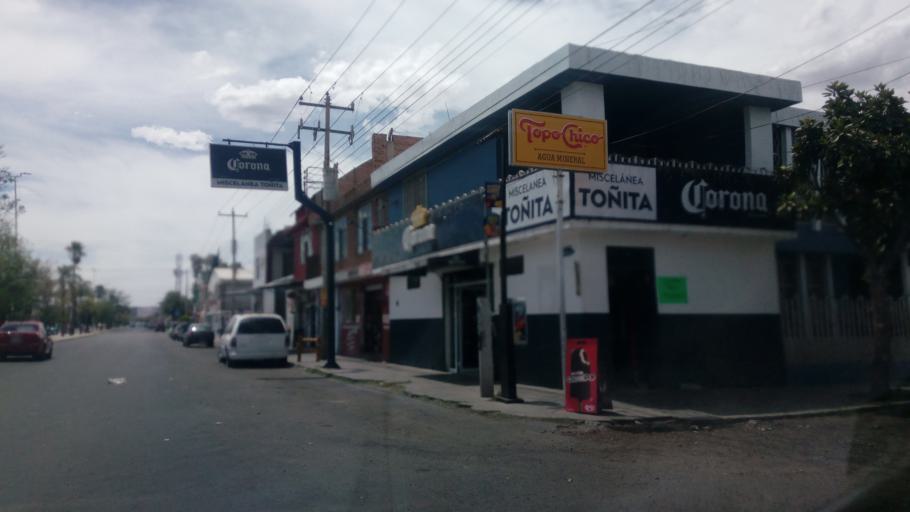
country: MX
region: Durango
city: Victoria de Durango
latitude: 23.9967
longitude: -104.6698
